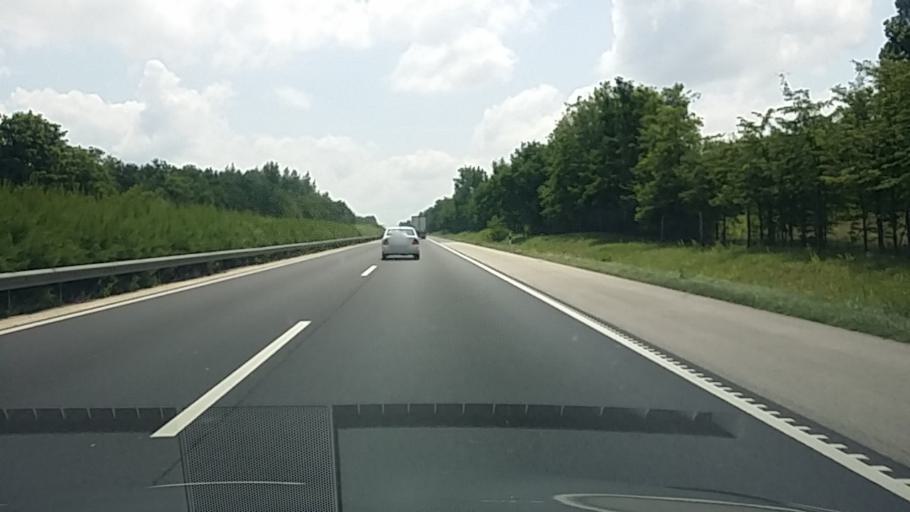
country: HU
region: Pest
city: Inarcs
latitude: 47.2905
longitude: 19.3018
